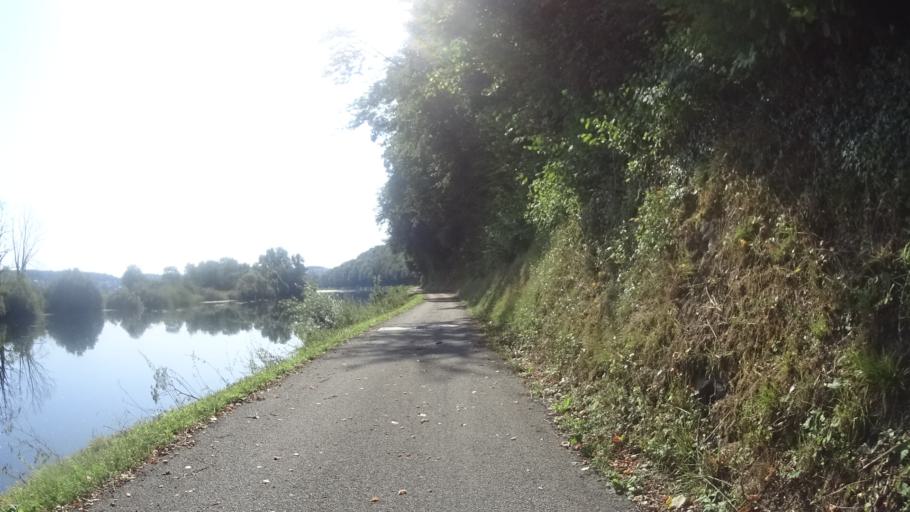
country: FR
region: Franche-Comte
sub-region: Departement du Doubs
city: Clerval
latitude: 47.4314
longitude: 6.5351
